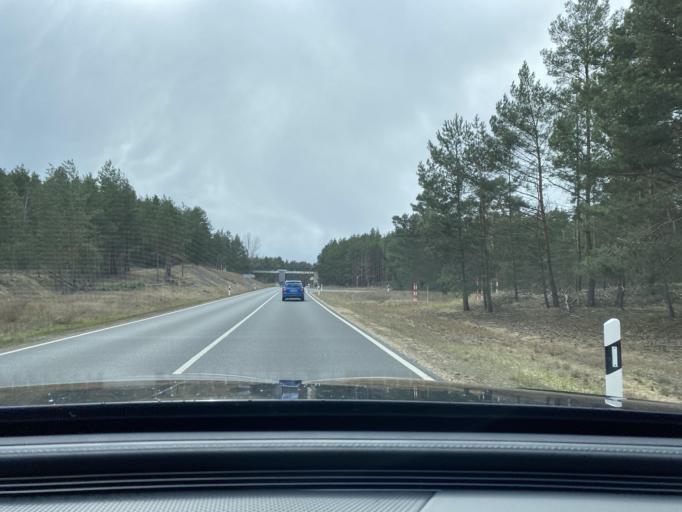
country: DE
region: Saxony
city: Boxberg
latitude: 51.4152
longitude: 14.5899
